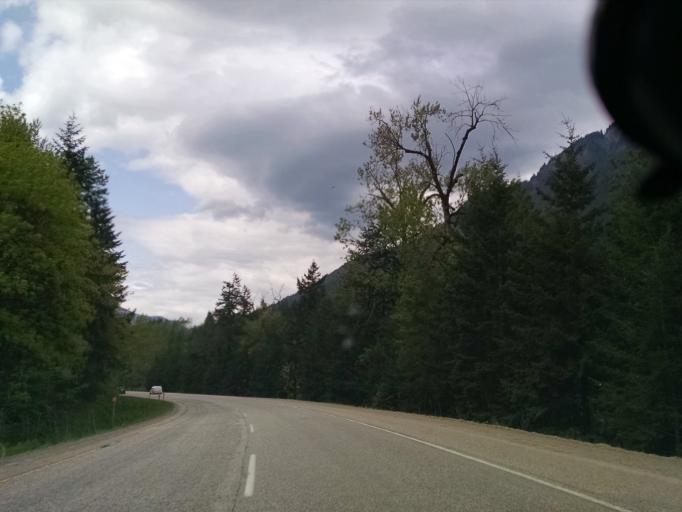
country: CA
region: British Columbia
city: Hope
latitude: 49.3788
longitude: -121.3511
